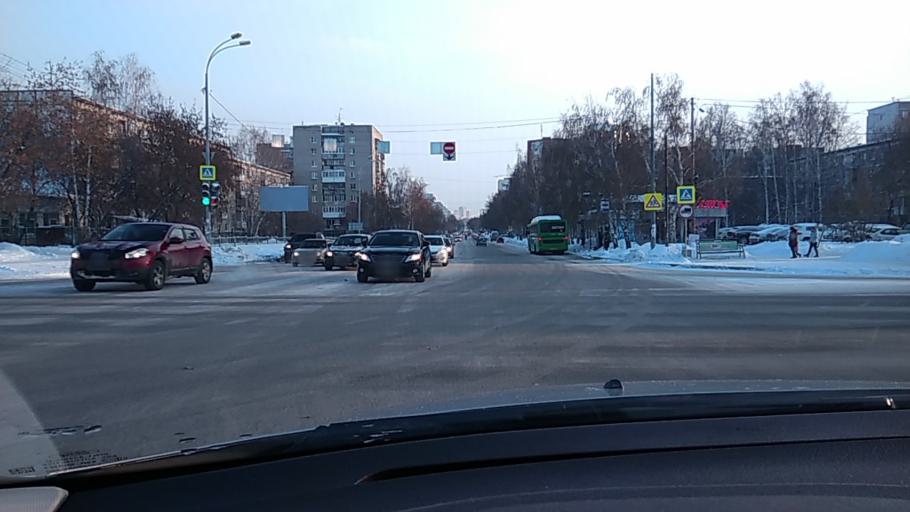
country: RU
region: Sverdlovsk
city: Sovkhoznyy
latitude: 56.8192
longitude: 60.5574
